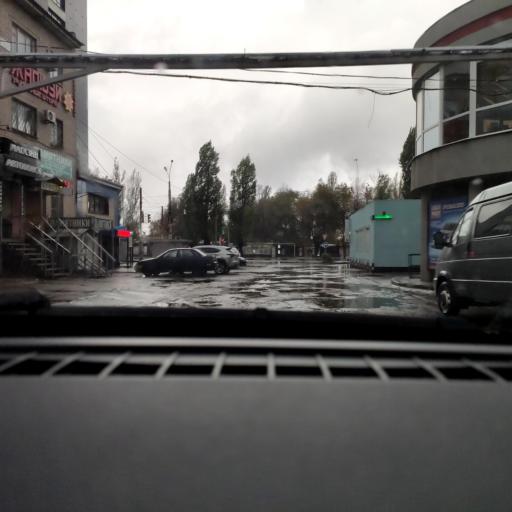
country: RU
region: Voronezj
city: Voronezh
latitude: 51.7005
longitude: 39.2751
